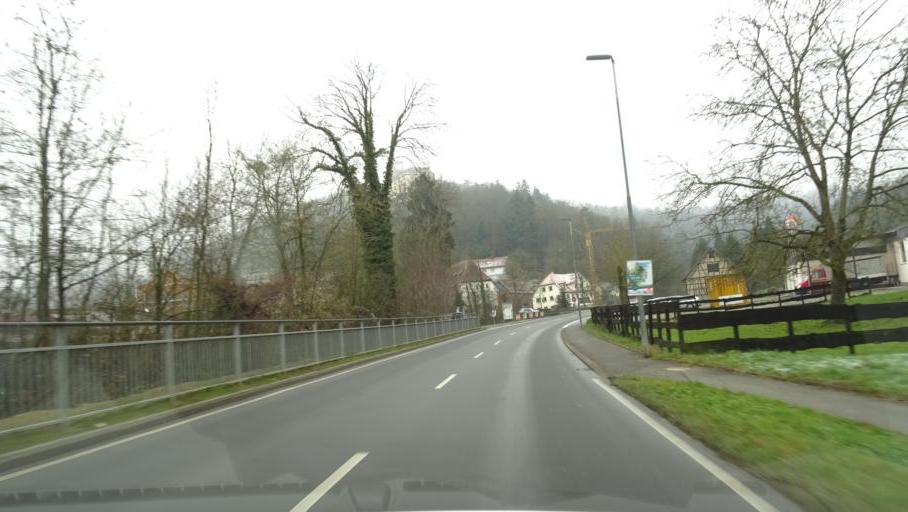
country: DE
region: Baden-Wuerttemberg
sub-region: Karlsruhe Region
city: Hassmersheim
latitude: 49.2844
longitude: 9.1332
